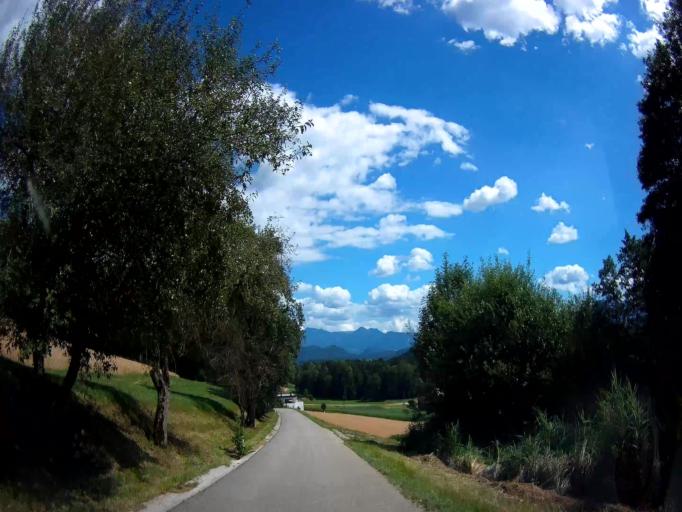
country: AT
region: Carinthia
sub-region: Politischer Bezirk Klagenfurt Land
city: Poggersdorf
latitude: 46.6623
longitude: 14.5371
